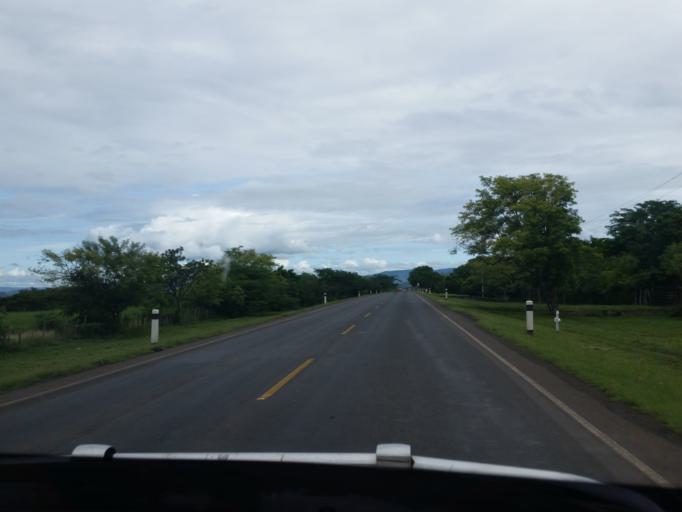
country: NI
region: Managua
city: Tipitapa
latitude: 12.3469
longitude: -86.0500
